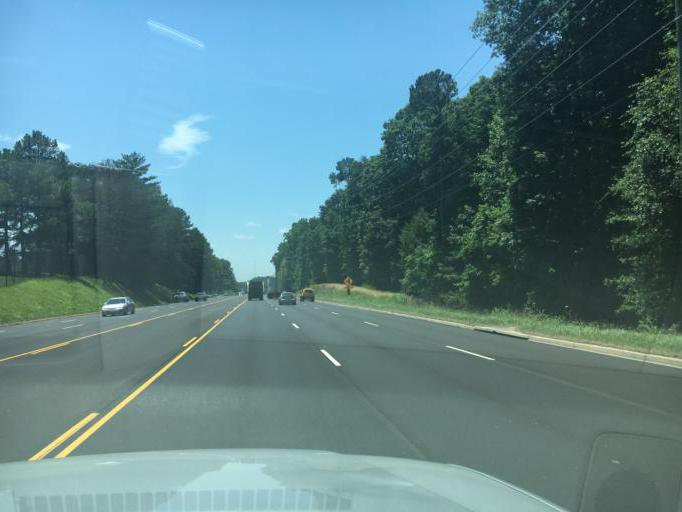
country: US
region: South Carolina
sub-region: Greenville County
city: Travelers Rest
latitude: 34.9314
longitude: -82.4510
